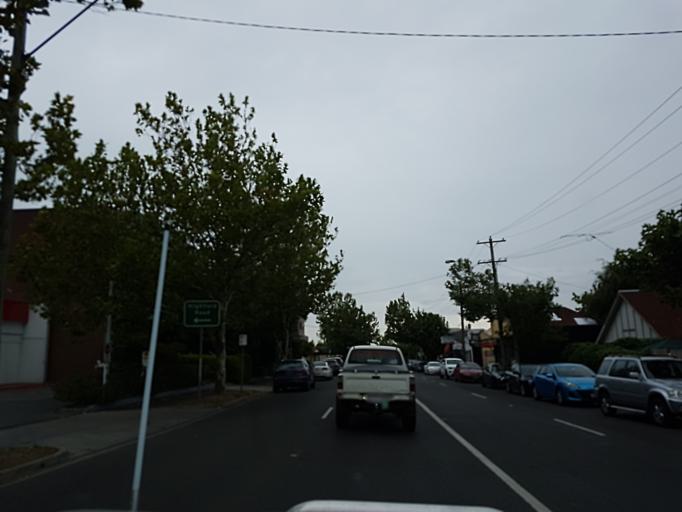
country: AU
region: Victoria
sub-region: Boroondara
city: Canterbury
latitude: -37.8248
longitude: 145.0877
